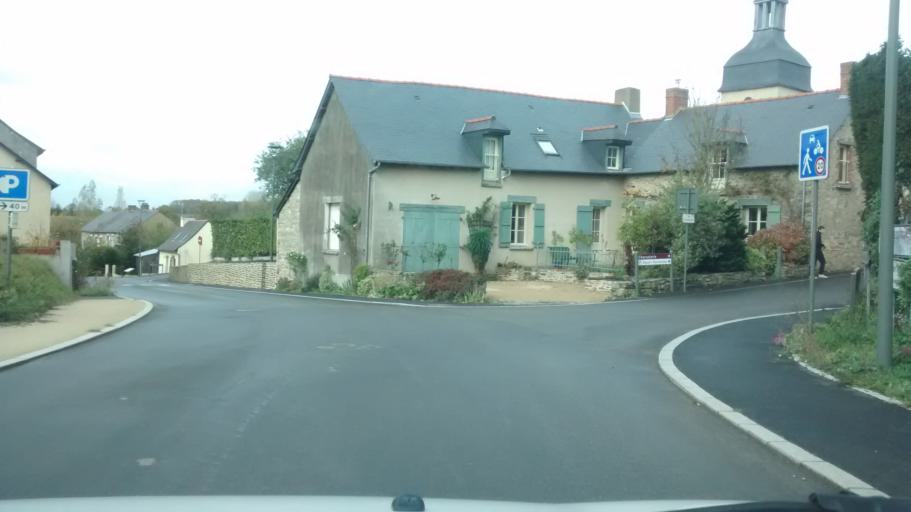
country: FR
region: Brittany
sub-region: Departement d'Ille-et-Vilaine
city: Chateaubourg
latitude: 48.1300
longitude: -1.4215
